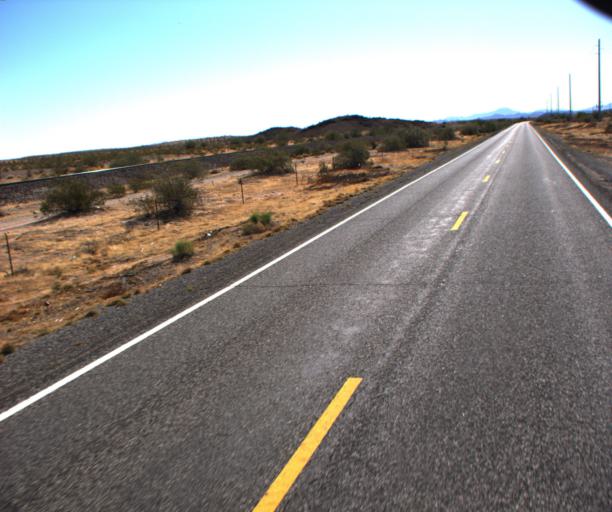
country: US
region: Arizona
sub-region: La Paz County
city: Cienega Springs
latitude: 33.9924
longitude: -114.0866
